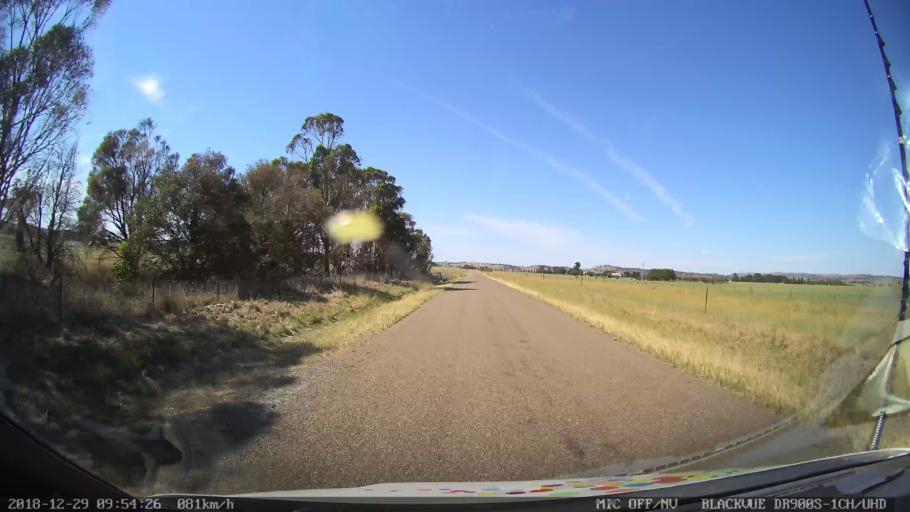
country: AU
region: New South Wales
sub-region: Goulburn Mulwaree
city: Goulburn
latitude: -34.7632
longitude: 149.4671
